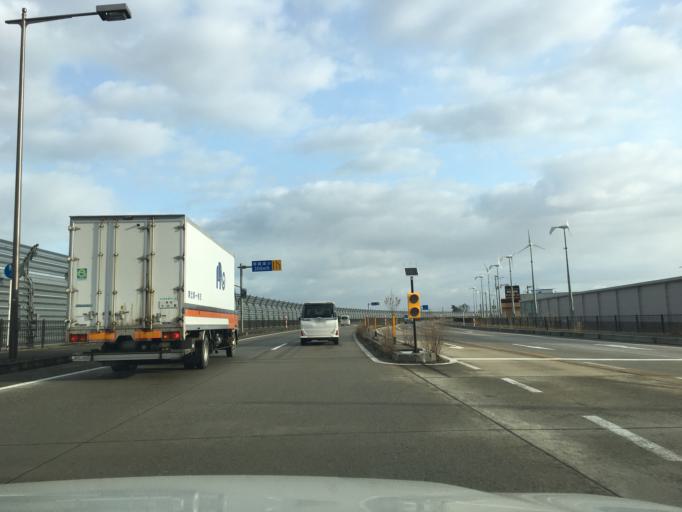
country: JP
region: Yamagata
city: Tsuruoka
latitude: 38.8186
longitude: 139.8326
